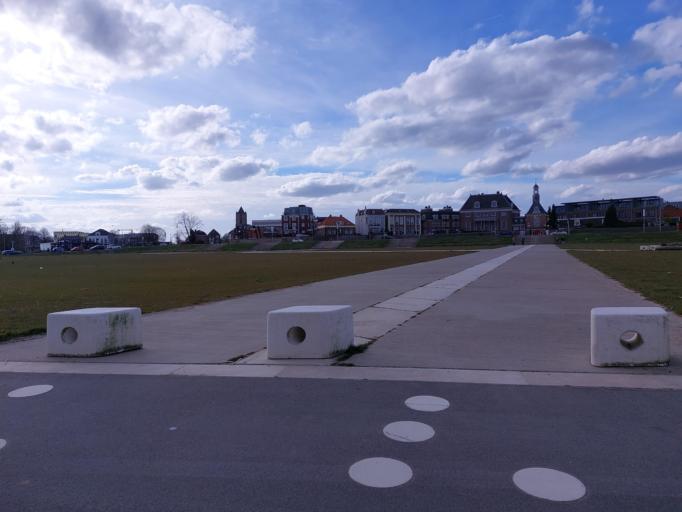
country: NL
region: Gelderland
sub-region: Gemeente Tiel
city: Tiel
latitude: 51.8858
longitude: 5.4423
